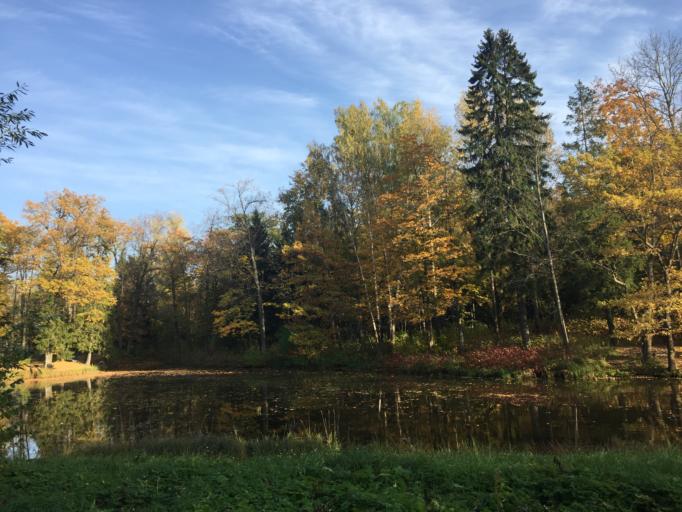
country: RU
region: St.-Petersburg
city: Pushkin
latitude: 59.7212
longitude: 30.3719
